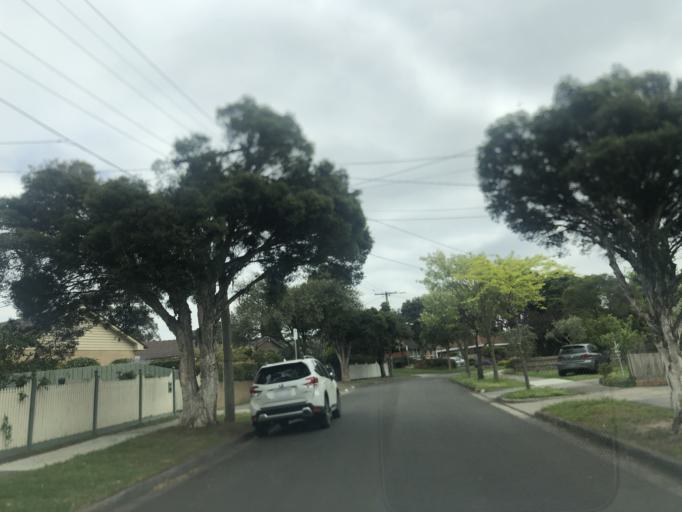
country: AU
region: Victoria
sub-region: Monash
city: Notting Hill
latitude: -37.9092
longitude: 145.1632
